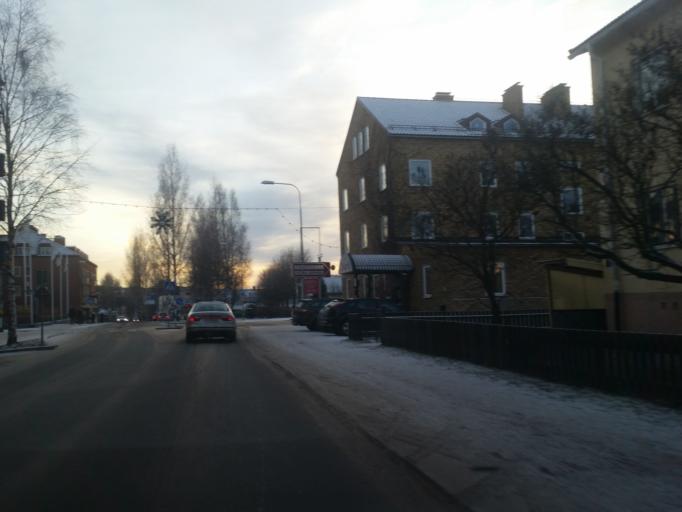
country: SE
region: Dalarna
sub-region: Leksand Municipality
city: Leksand
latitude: 60.7331
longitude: 14.9972
